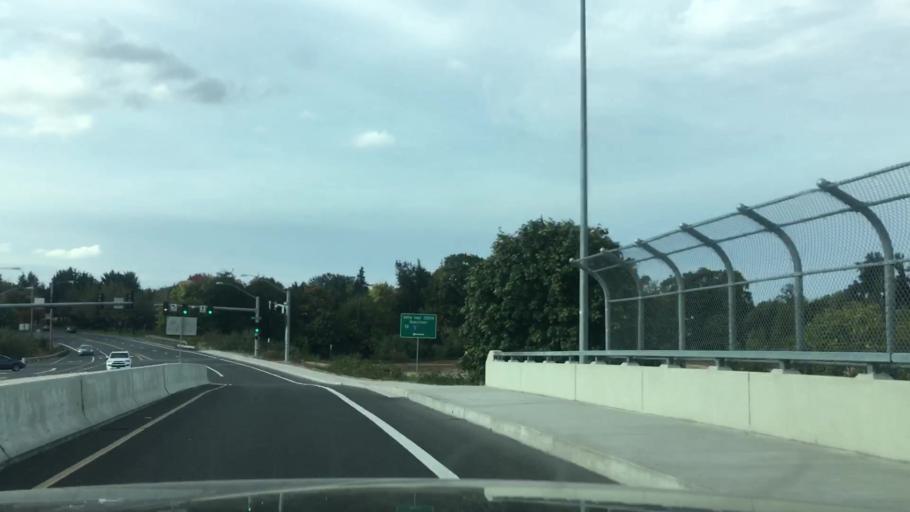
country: US
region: Oregon
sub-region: Lane County
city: Eugene
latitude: 44.0853
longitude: -123.1023
